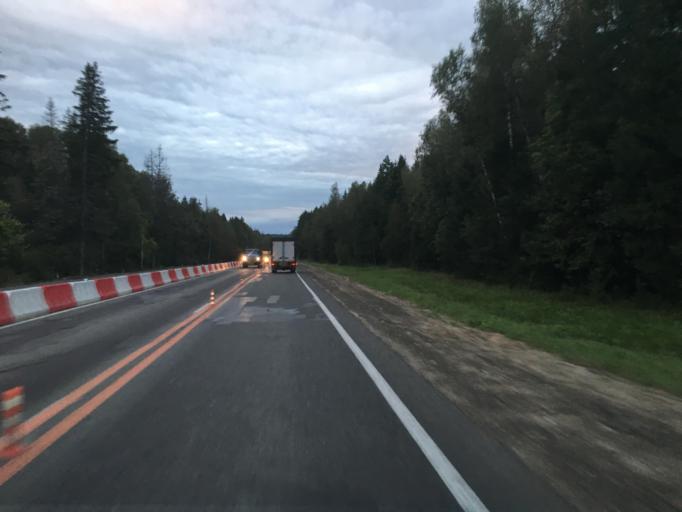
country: RU
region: Kaluga
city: Detchino
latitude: 54.6988
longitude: 36.2937
